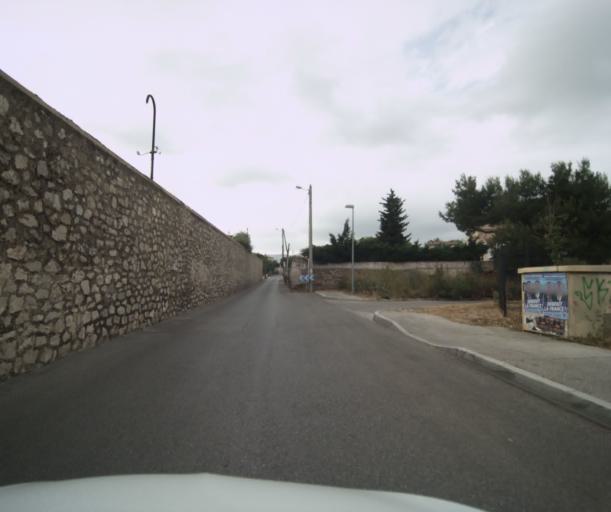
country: FR
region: Provence-Alpes-Cote d'Azur
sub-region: Departement du Var
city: La Seyne-sur-Mer
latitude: 43.1187
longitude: 5.8808
